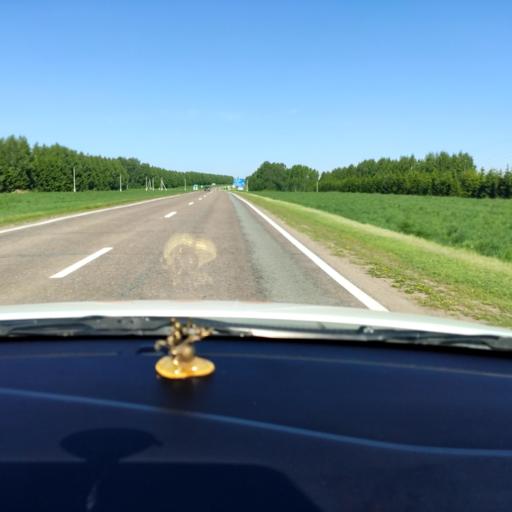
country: RU
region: Tatarstan
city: Vysokaya Gora
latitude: 56.0321
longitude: 49.2415
